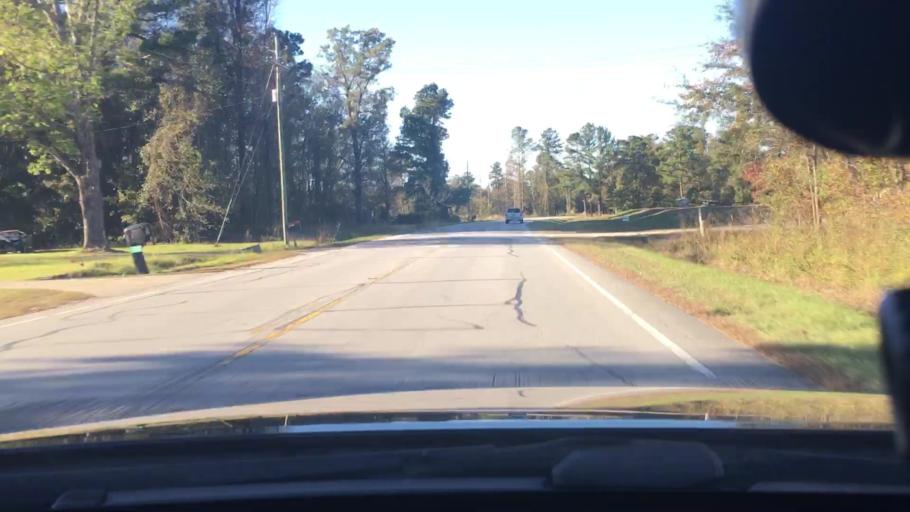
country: US
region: North Carolina
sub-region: Craven County
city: Vanceboro
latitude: 35.3277
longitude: -77.1697
